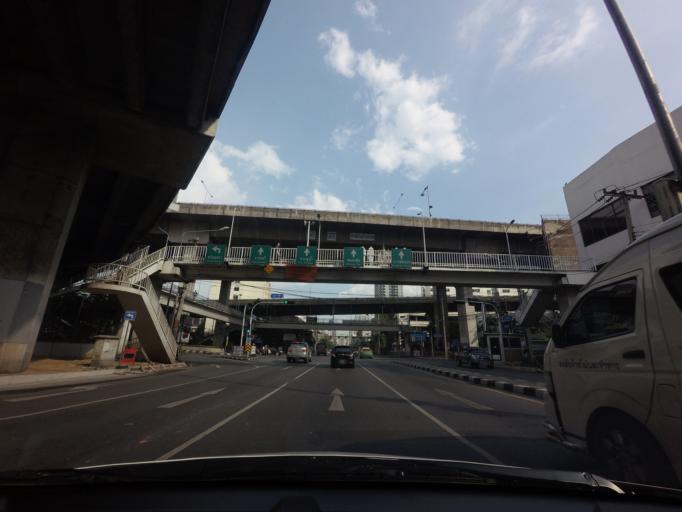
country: TH
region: Bangkok
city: Pom Prap Sattru Phai
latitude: 13.7563
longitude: 100.5232
